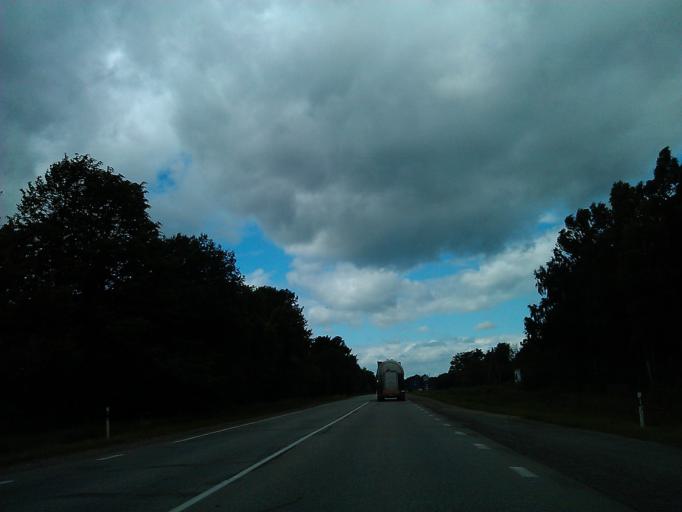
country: LV
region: Tukuma Rajons
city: Tukums
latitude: 56.9310
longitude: 23.2097
